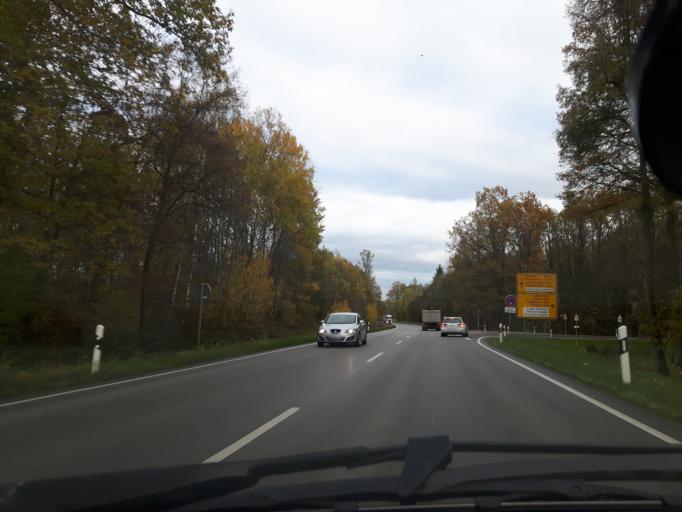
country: DE
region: Bavaria
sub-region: Regierungsbezirk Mittelfranken
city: Weidenbach
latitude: 49.2135
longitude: 10.6456
